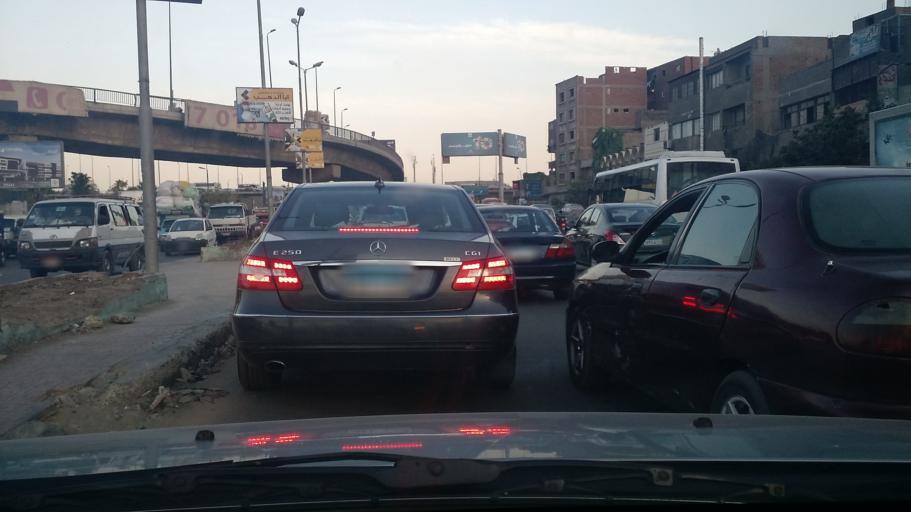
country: EG
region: Al Jizah
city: Al Jizah
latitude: 29.9937
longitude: 31.2817
